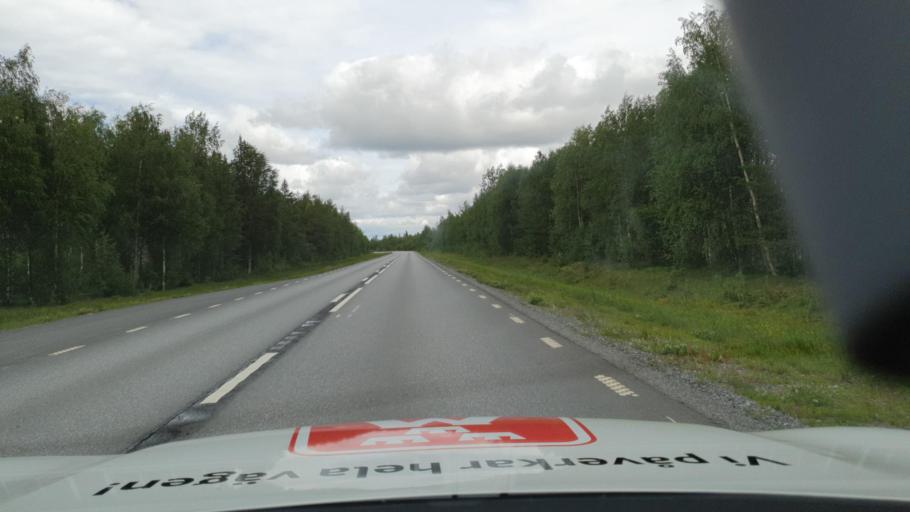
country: SE
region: Vaesterbotten
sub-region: Dorotea Kommun
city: Dorotea
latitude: 64.3321
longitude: 16.6355
